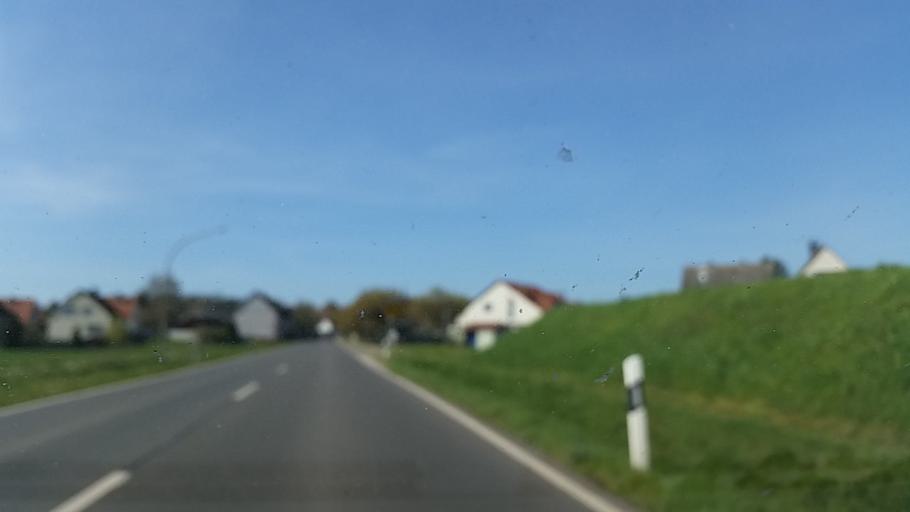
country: DE
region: Lower Saxony
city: Jerxheim
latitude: 52.0854
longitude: 10.9089
